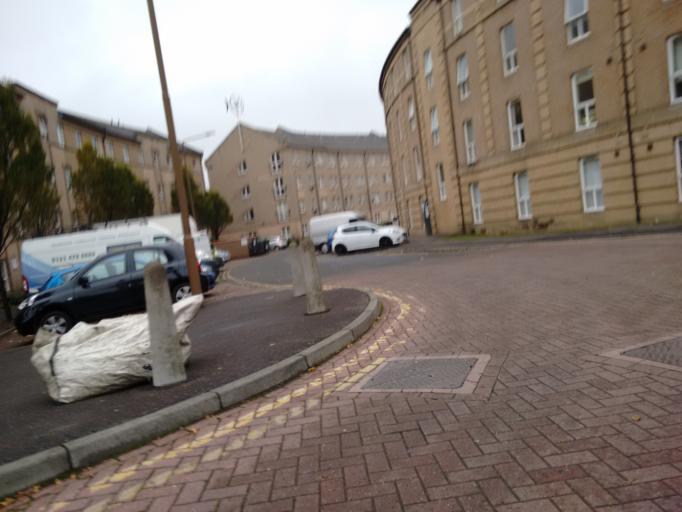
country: GB
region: Scotland
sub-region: Edinburgh
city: Edinburgh
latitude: 55.9441
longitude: -3.2145
